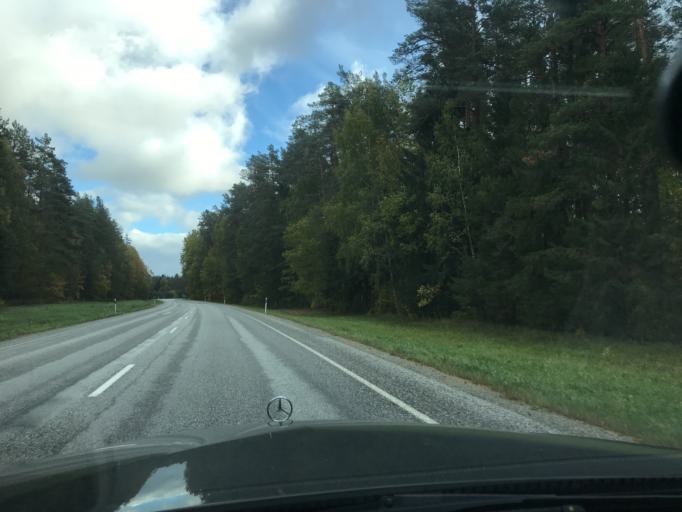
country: EE
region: Vorumaa
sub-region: Voru linn
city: Voru
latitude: 57.7378
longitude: 27.2843
